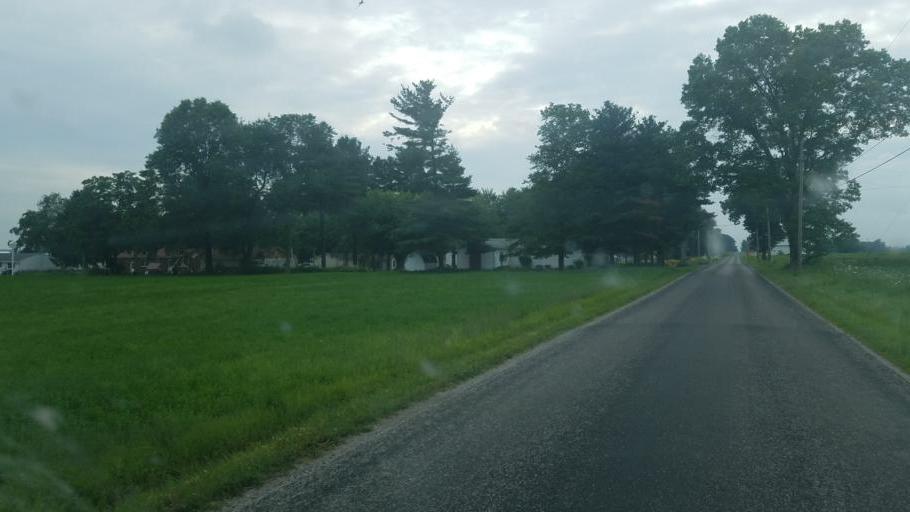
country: US
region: Ohio
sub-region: Wayne County
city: Apple Creek
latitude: 40.7775
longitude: -81.8381
